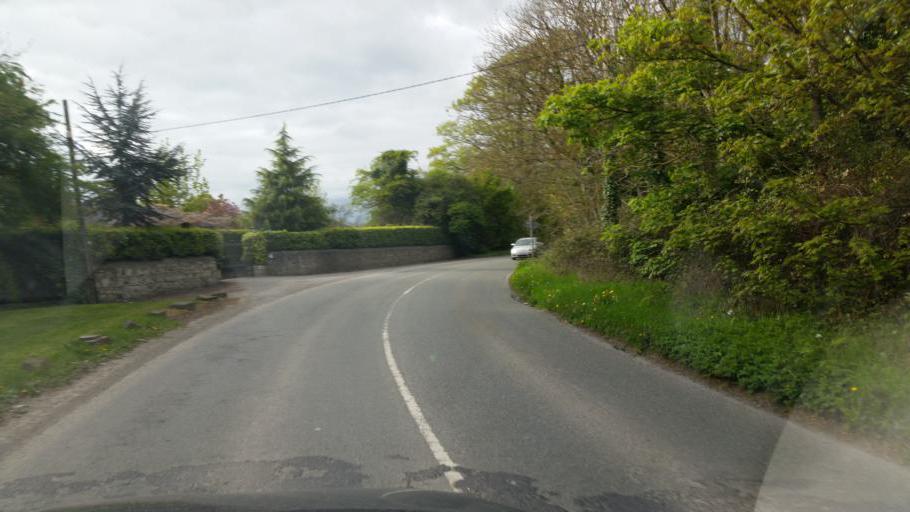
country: IE
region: Leinster
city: Hartstown
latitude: 53.3993
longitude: -6.4432
